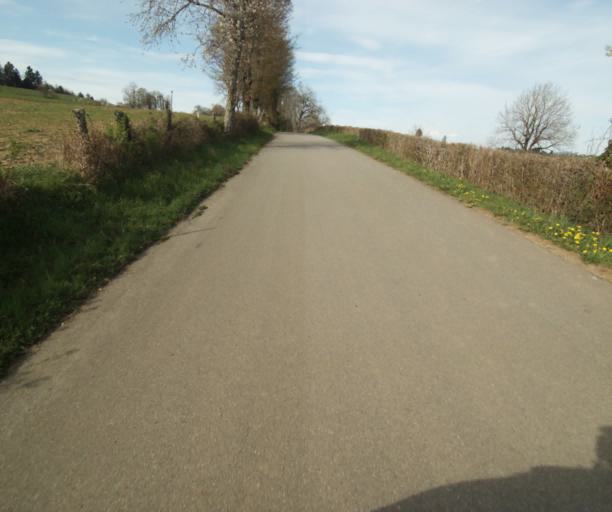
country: FR
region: Limousin
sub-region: Departement de la Correze
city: Naves
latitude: 45.3250
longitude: 1.7306
